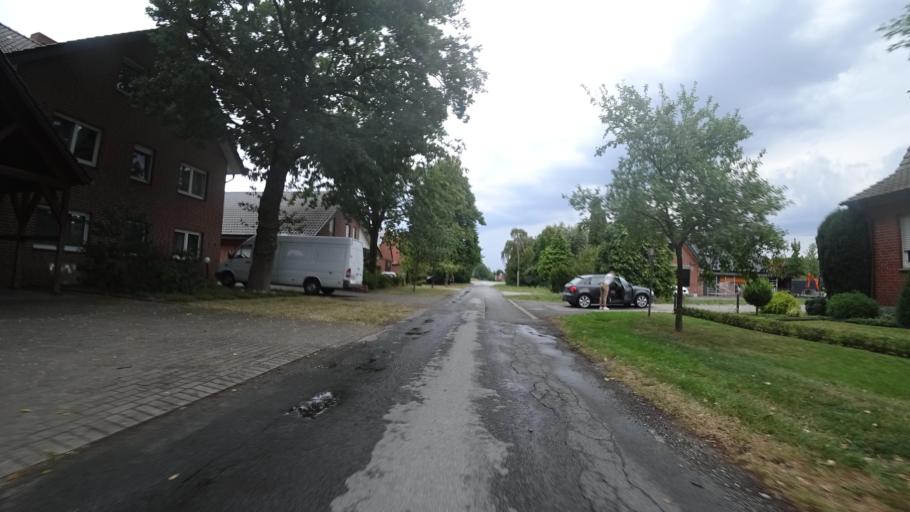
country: DE
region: North Rhine-Westphalia
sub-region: Regierungsbezirk Detmold
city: Rheda-Wiedenbruck
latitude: 51.8931
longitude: 8.2945
